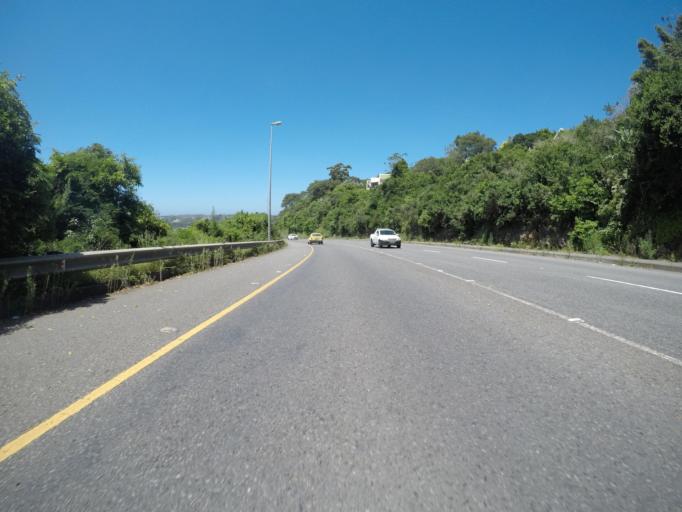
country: ZA
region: Eastern Cape
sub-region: Buffalo City Metropolitan Municipality
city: East London
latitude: -32.9679
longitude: 27.9307
